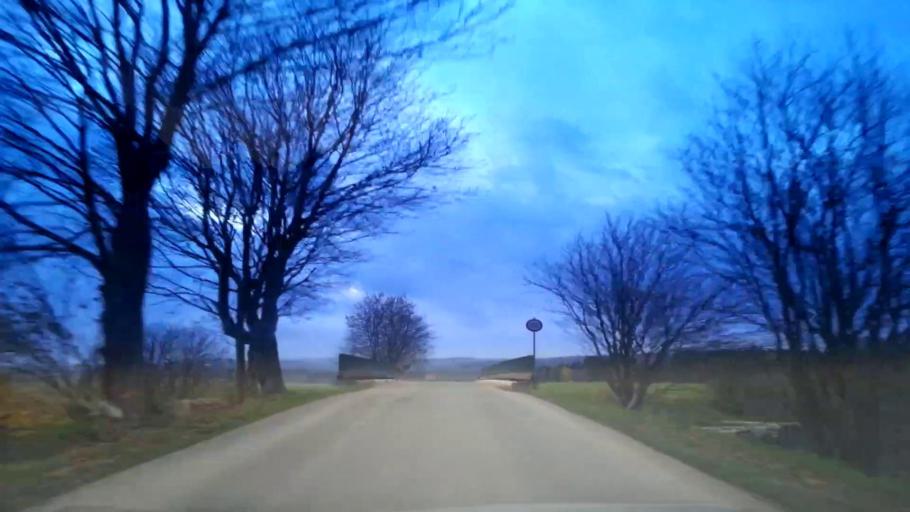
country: DE
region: Bavaria
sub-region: Upper Palatinate
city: Pechbrunn
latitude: 49.9419
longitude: 12.1878
